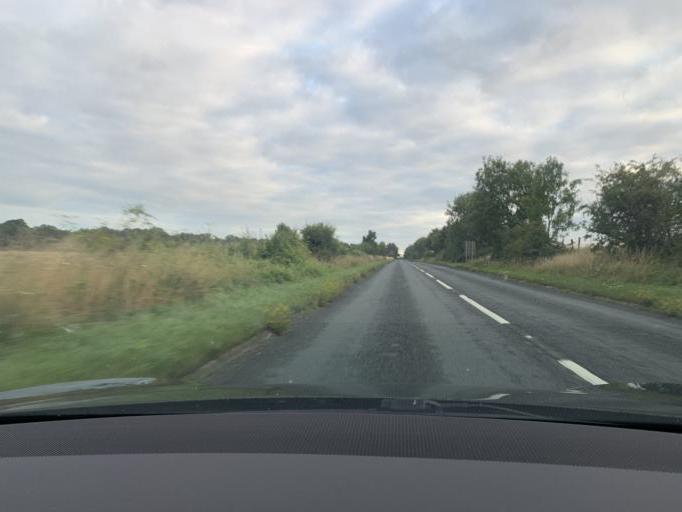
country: GB
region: England
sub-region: Wiltshire
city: Tidworth
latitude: 51.2509
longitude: -1.6661
